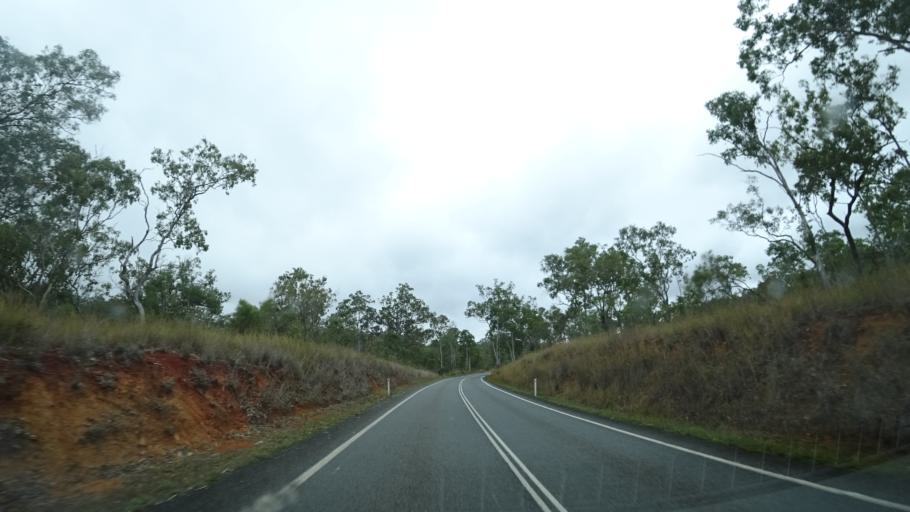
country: AU
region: Queensland
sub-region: Cairns
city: Port Douglas
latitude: -16.6966
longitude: 145.3453
